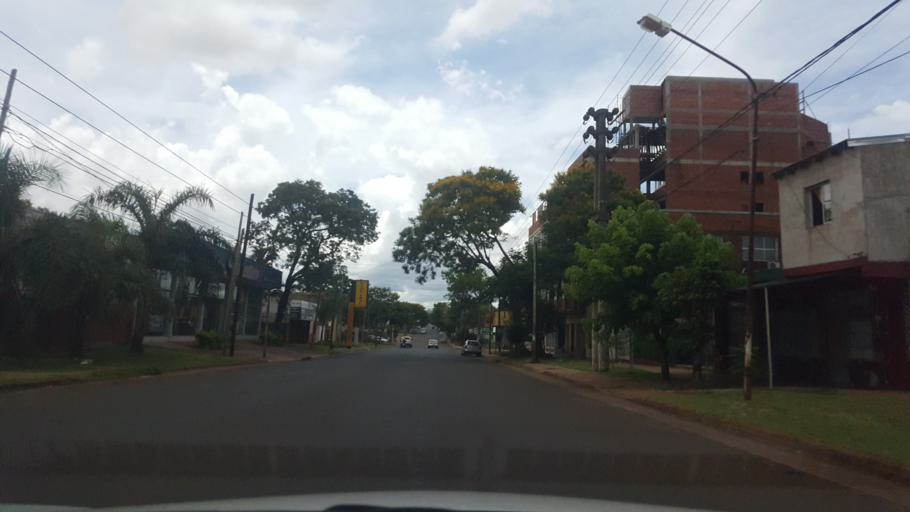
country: AR
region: Misiones
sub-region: Departamento de Capital
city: Posadas
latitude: -27.3960
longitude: -55.8977
